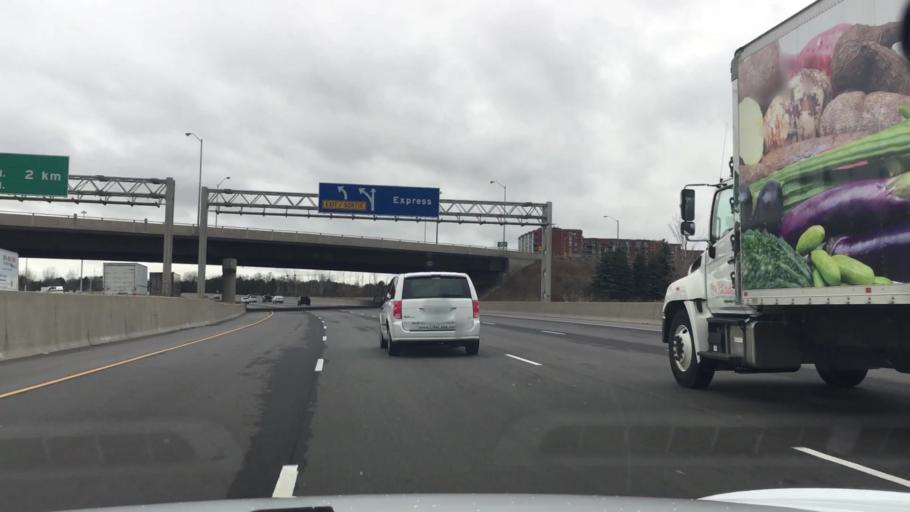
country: CA
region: Ontario
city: Scarborough
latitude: 43.7994
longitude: -79.1649
